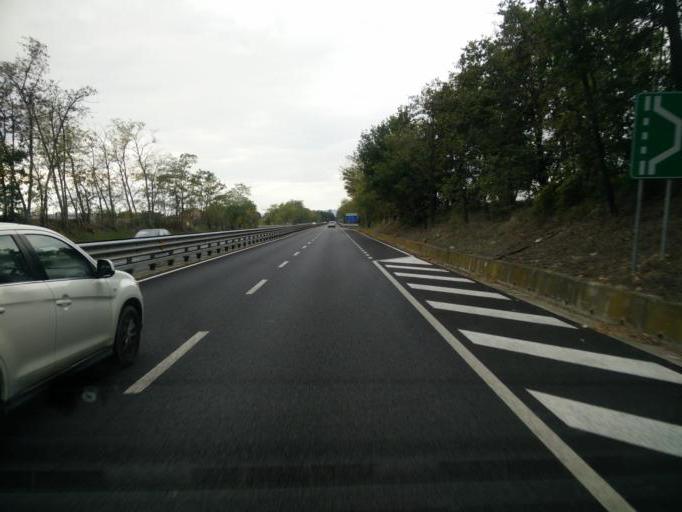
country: IT
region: Tuscany
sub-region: Provincia di Siena
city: Staggia
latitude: 43.4085
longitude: 11.1745
